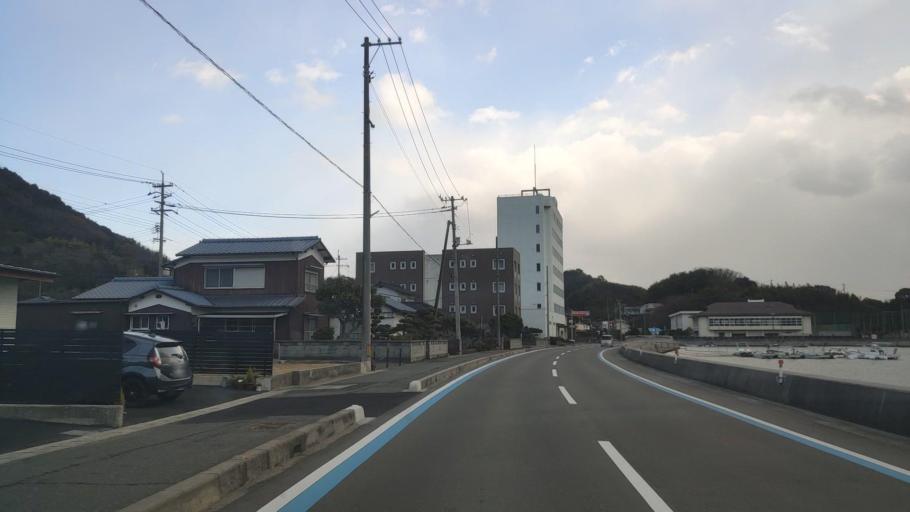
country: JP
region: Hiroshima
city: Innoshima
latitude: 34.2044
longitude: 133.0988
